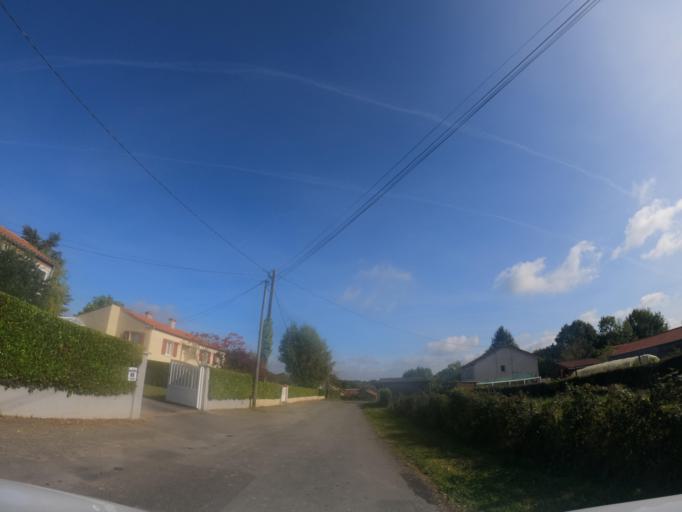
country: FR
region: Poitou-Charentes
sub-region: Departement des Deux-Sevres
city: Courlay
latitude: 46.7855
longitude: -0.5666
